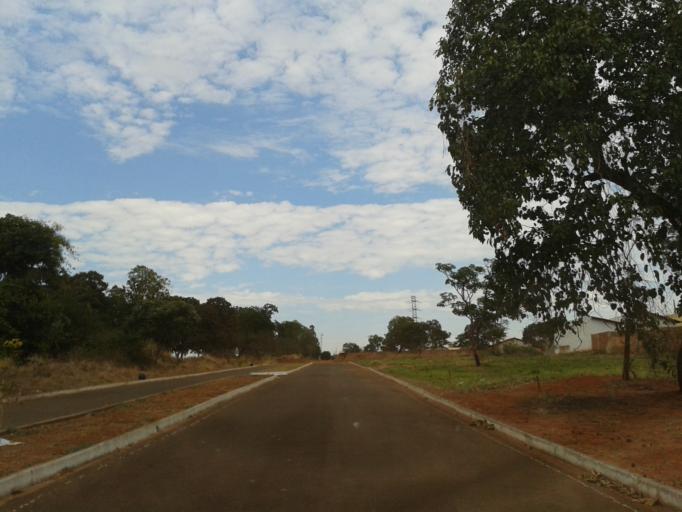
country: BR
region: Minas Gerais
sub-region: Santa Vitoria
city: Santa Vitoria
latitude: -18.8551
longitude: -50.1174
